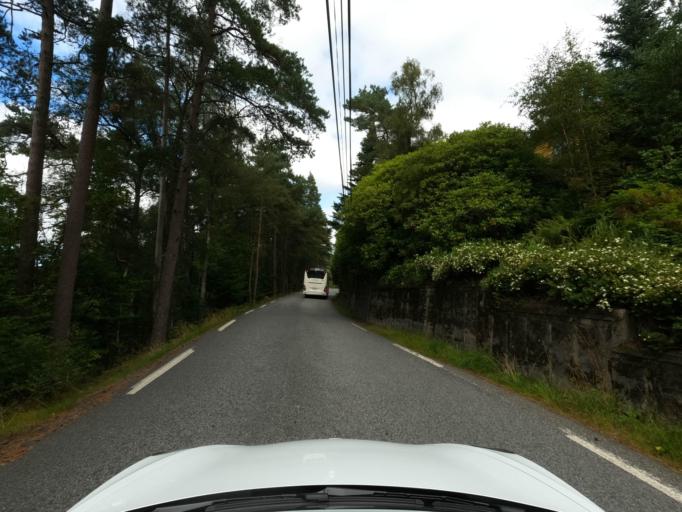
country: NO
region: Hordaland
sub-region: Os
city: Hagavik
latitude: 60.2028
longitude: 5.3800
